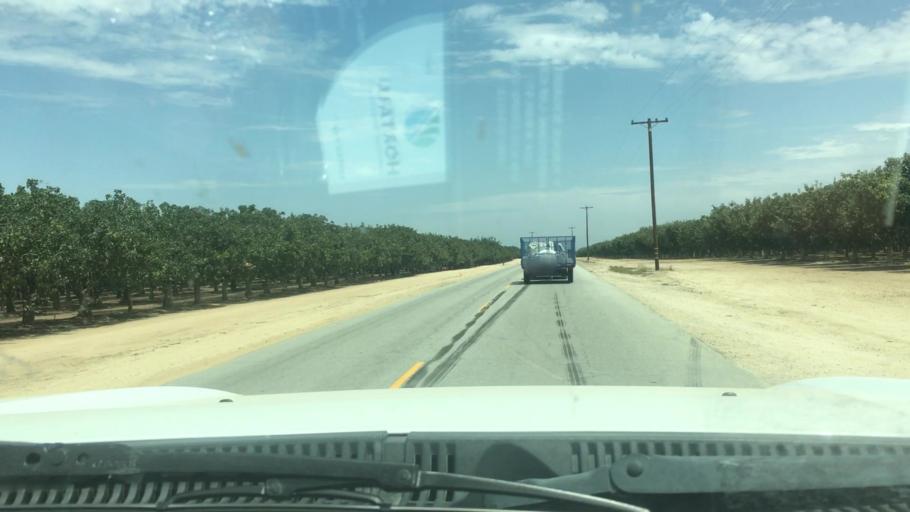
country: US
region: California
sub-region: Kern County
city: McFarland
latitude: 35.5950
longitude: -119.1510
